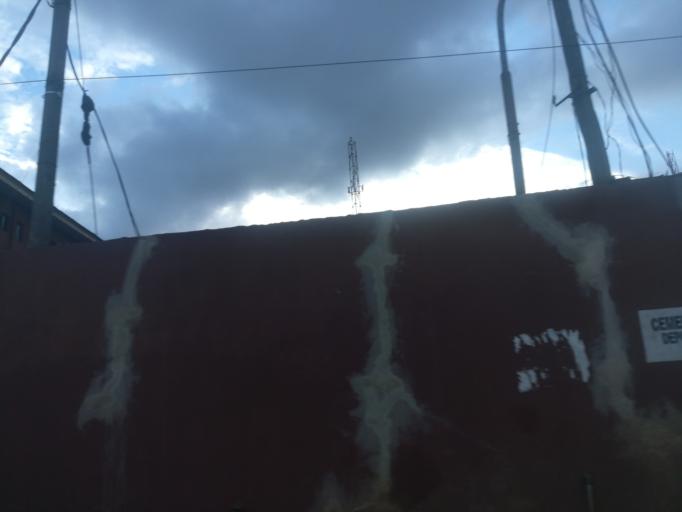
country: NG
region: Lagos
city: Ojota
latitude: 6.5641
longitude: 3.3687
